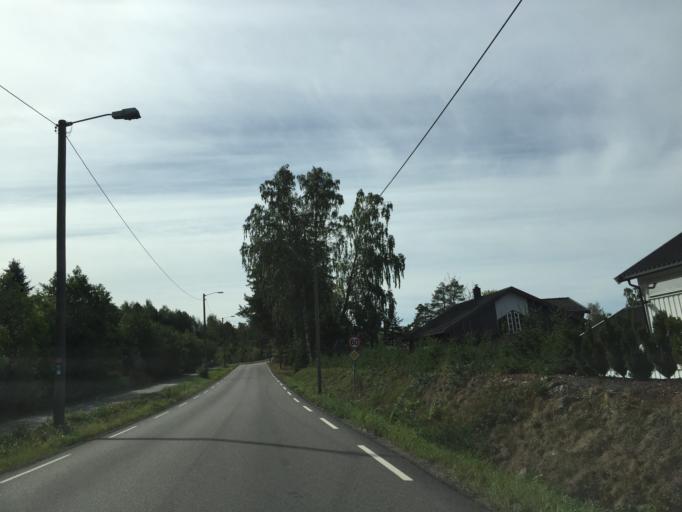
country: NO
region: Ostfold
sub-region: Moss
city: Moss
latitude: 59.5088
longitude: 10.6856
